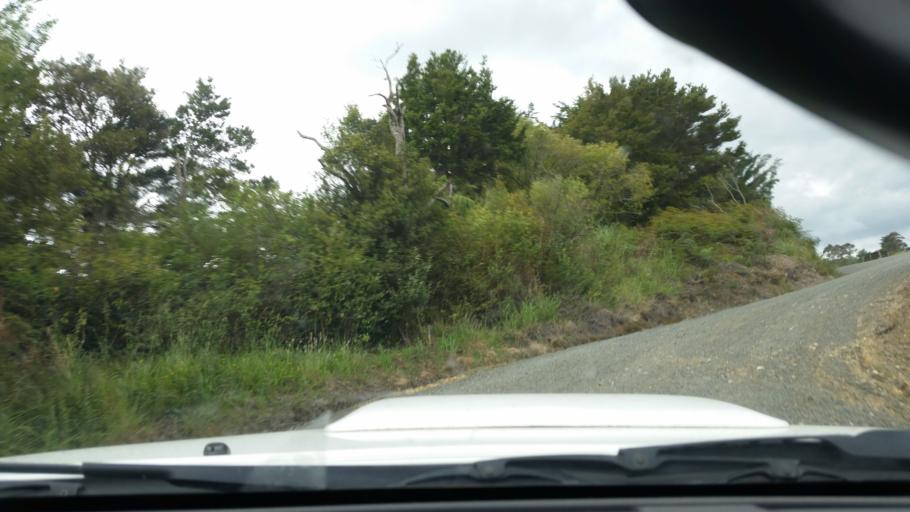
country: NZ
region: Northland
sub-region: Kaipara District
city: Dargaville
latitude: -35.8108
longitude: 173.9043
